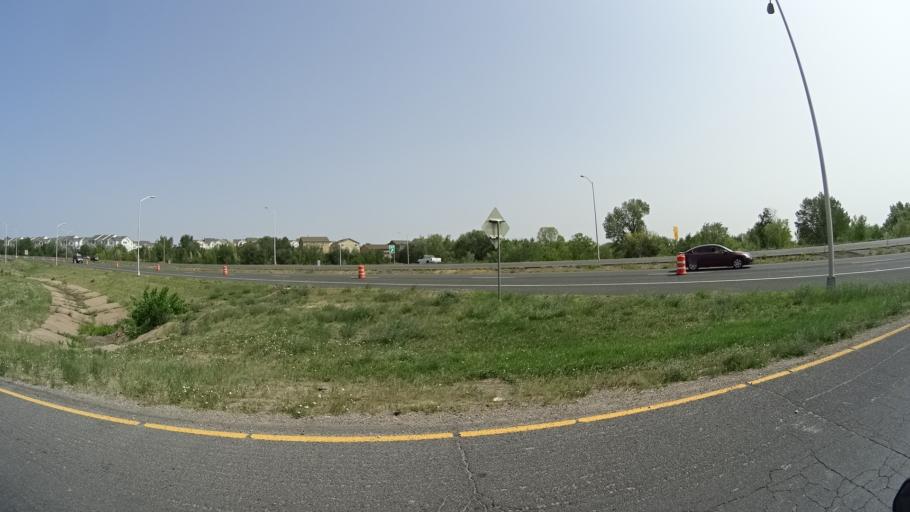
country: US
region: Colorado
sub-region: El Paso County
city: Stratmoor
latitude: 38.8001
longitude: -104.7815
